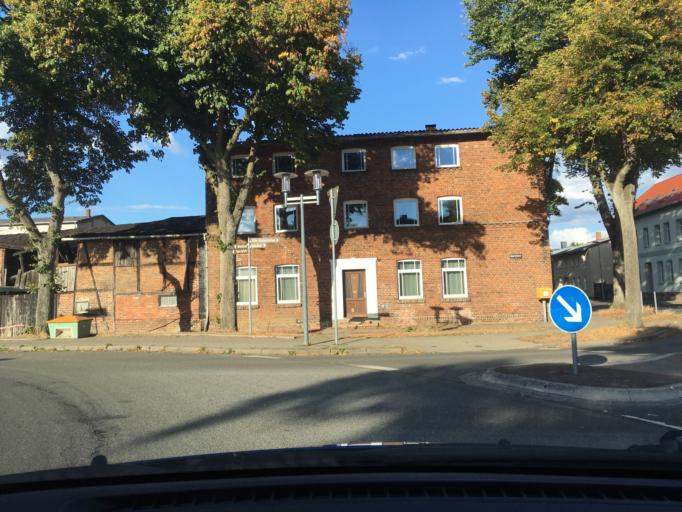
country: DE
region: Mecklenburg-Vorpommern
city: Grabow
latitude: 53.2827
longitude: 11.5585
